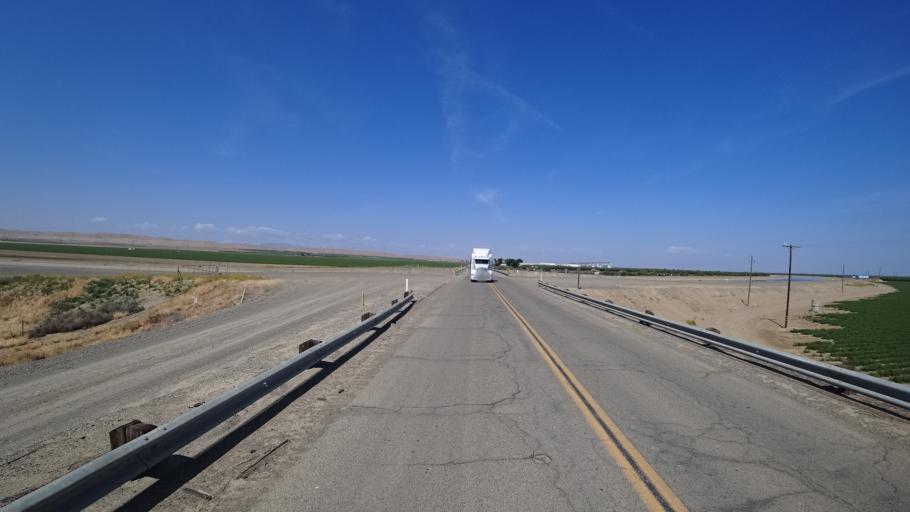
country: US
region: California
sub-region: Kings County
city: Kettleman City
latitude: 36.0724
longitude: -120.0214
